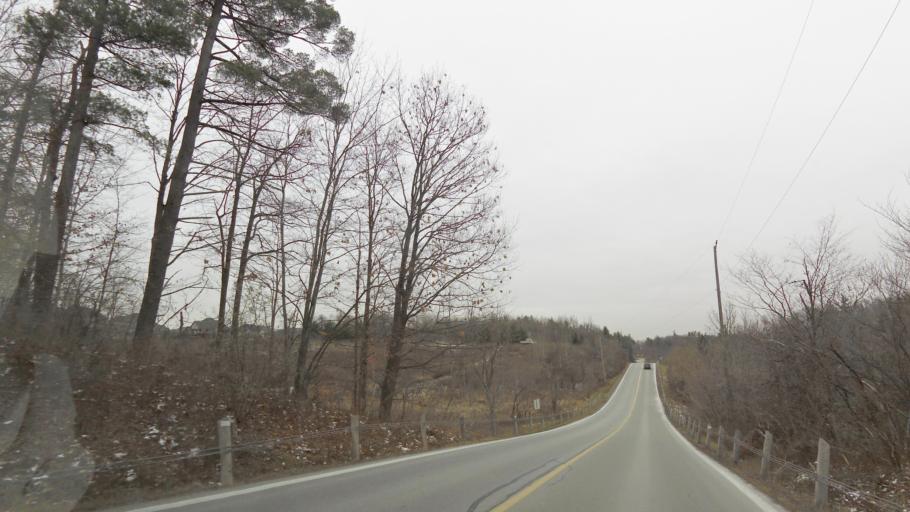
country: CA
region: Ontario
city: Vaughan
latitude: 43.8269
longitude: -79.5835
